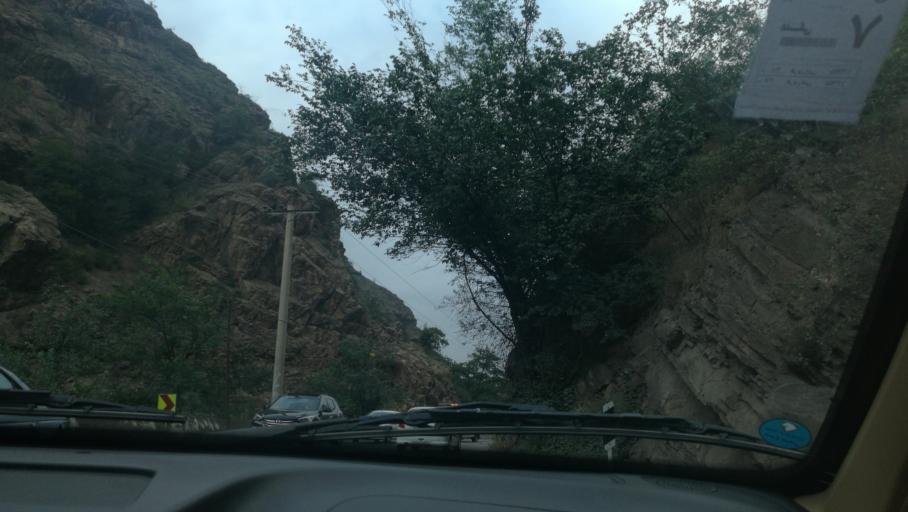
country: IR
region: Mazandaran
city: Chalus
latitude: 36.3221
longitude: 51.2528
